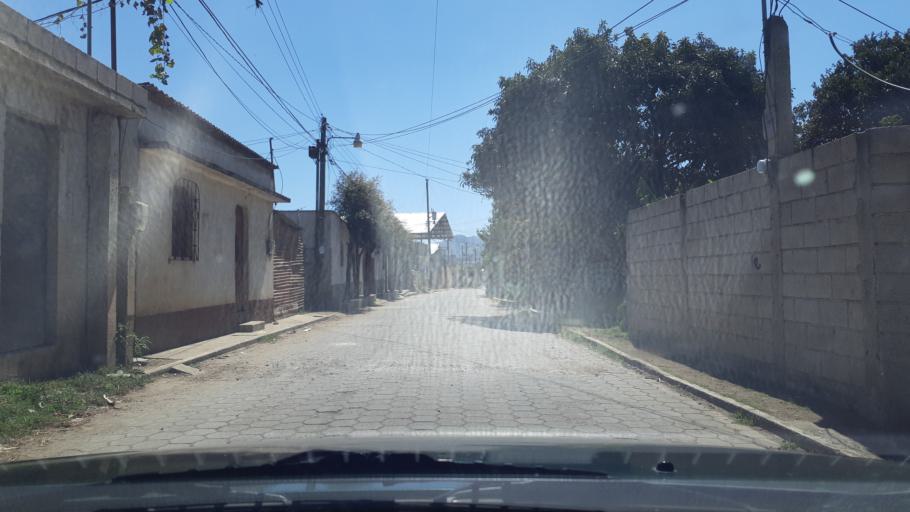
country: GT
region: Chimaltenango
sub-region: Municipio de Zaragoza
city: Zaragoza
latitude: 14.6628
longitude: -90.8634
